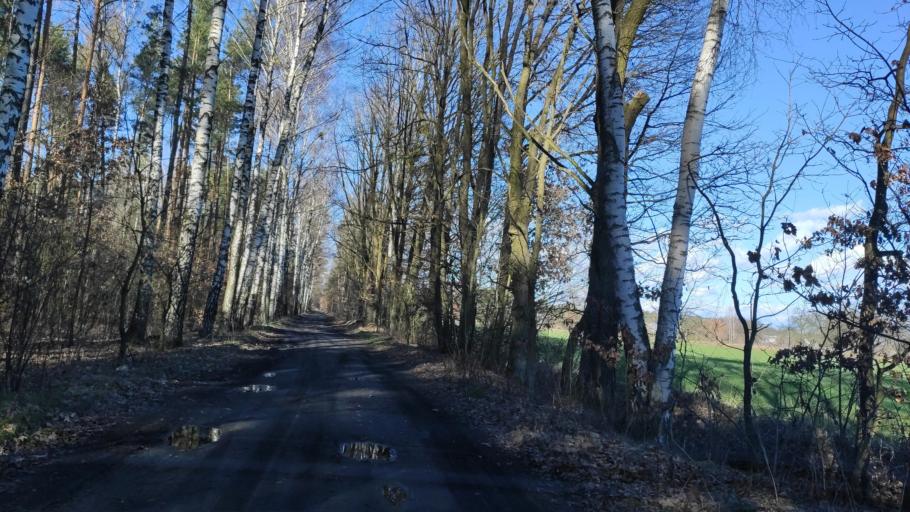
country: PL
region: Masovian Voivodeship
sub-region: Powiat radomski
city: Jedlnia-Letnisko
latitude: 51.4588
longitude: 21.3242
